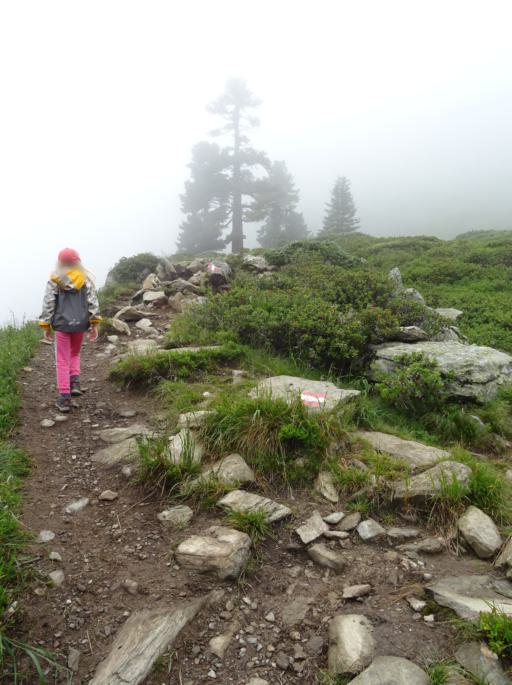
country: AT
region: Salzburg
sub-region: Politischer Bezirk Sankt Johann im Pongau
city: Forstau
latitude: 47.3456
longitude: 13.6007
